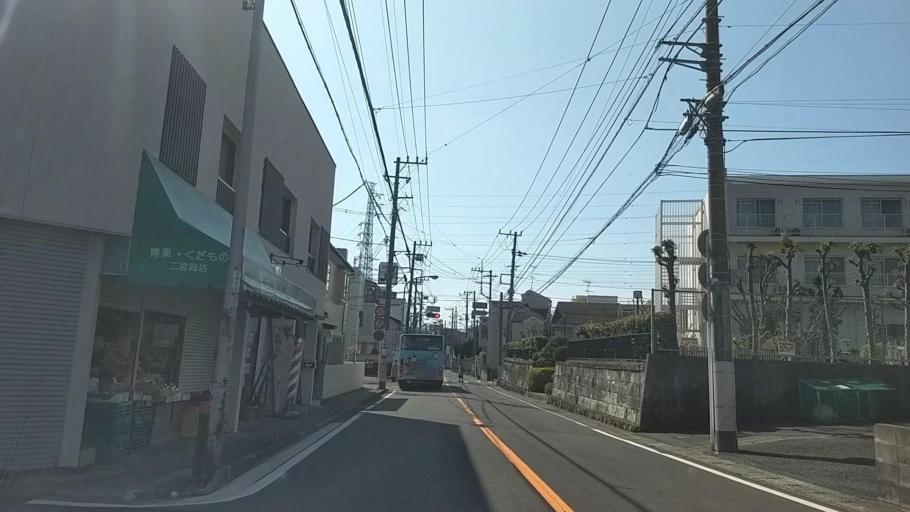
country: JP
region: Kanagawa
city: Kamakura
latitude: 35.3649
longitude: 139.5405
